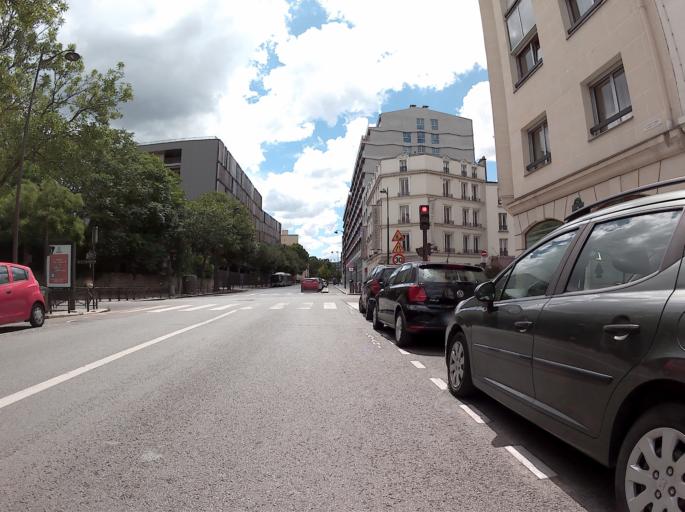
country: FR
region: Ile-de-France
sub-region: Departement du Val-de-Marne
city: Gentilly
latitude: 48.8240
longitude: 2.3310
